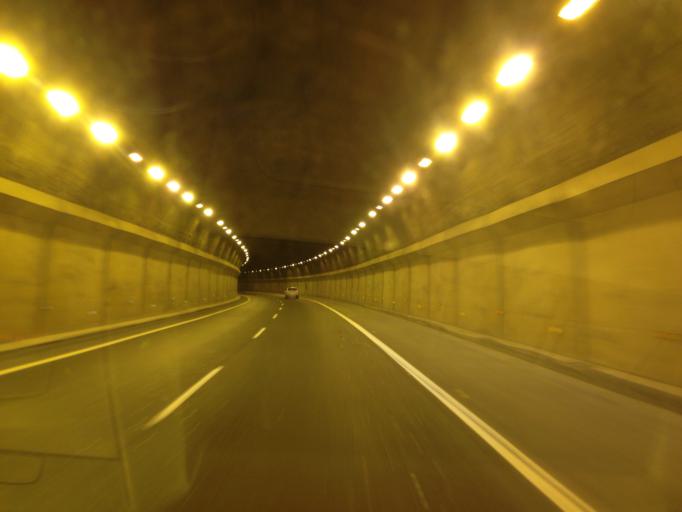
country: ES
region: Canary Islands
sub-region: Provincia de Las Palmas
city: Puerto Rico
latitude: 27.7705
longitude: -15.6584
